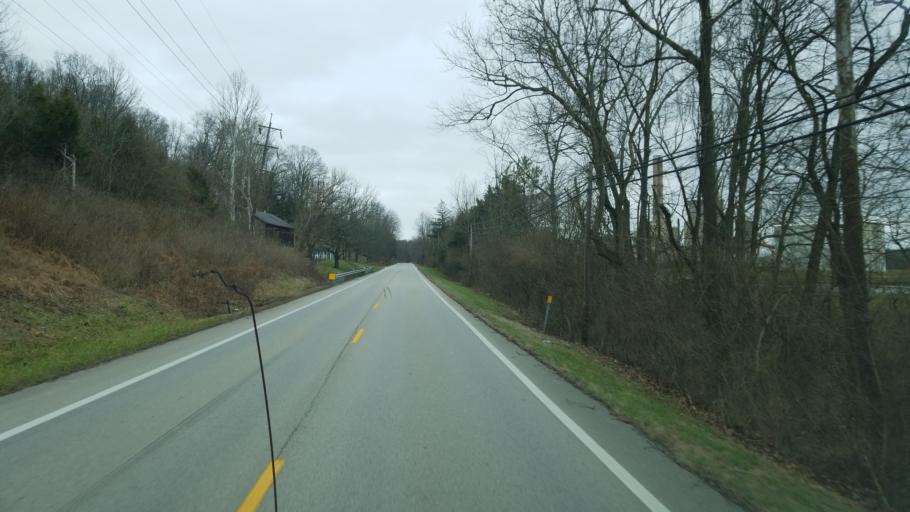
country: US
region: Ohio
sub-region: Clermont County
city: New Richmond
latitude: 38.8795
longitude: -84.2269
